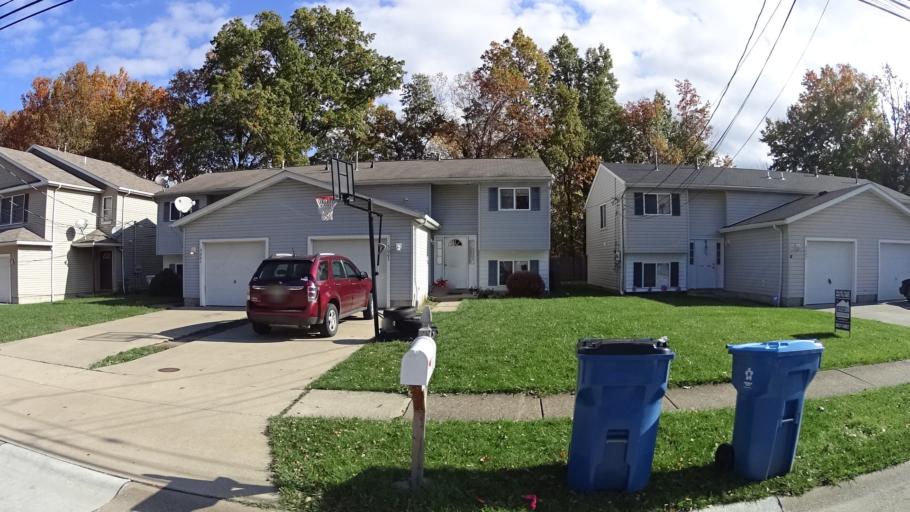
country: US
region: Ohio
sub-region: Lorain County
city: Lorain
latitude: 41.4430
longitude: -82.2242
